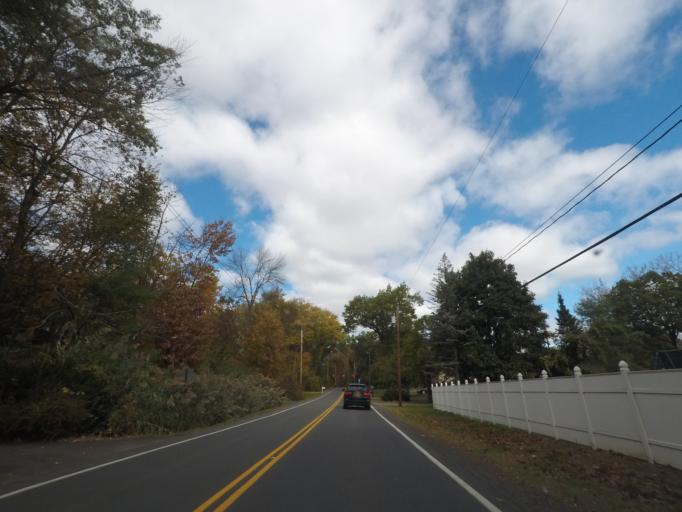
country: US
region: New York
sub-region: Saratoga County
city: Country Knolls
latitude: 42.8502
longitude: -73.7700
